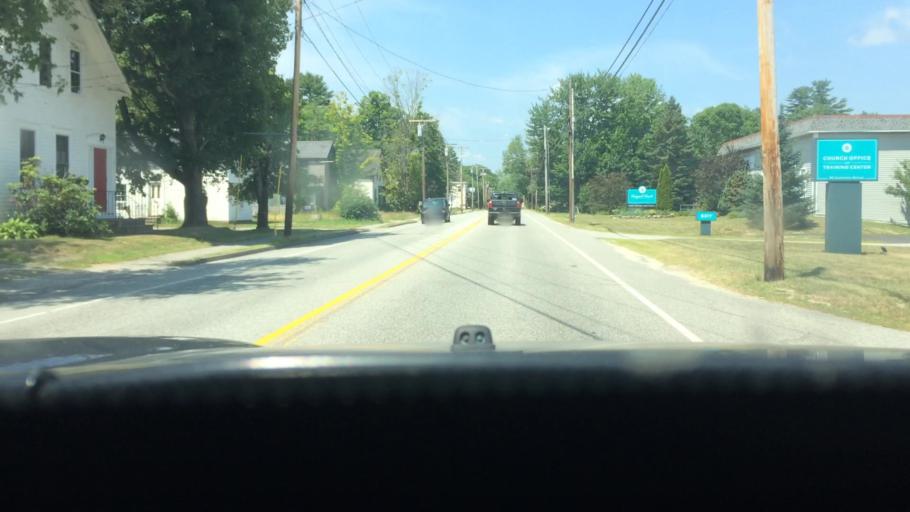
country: US
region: Maine
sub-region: Androscoggin County
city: Mechanic Falls
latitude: 44.1094
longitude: -70.3811
